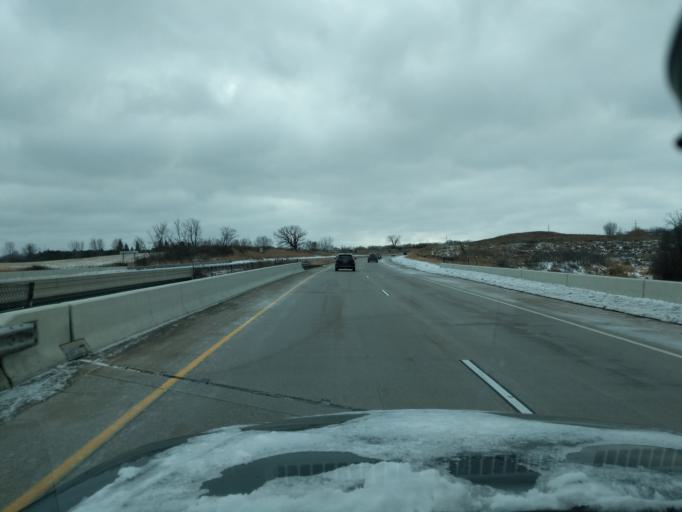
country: US
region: Minnesota
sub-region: Scott County
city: Shakopee
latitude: 44.8255
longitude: -93.5628
